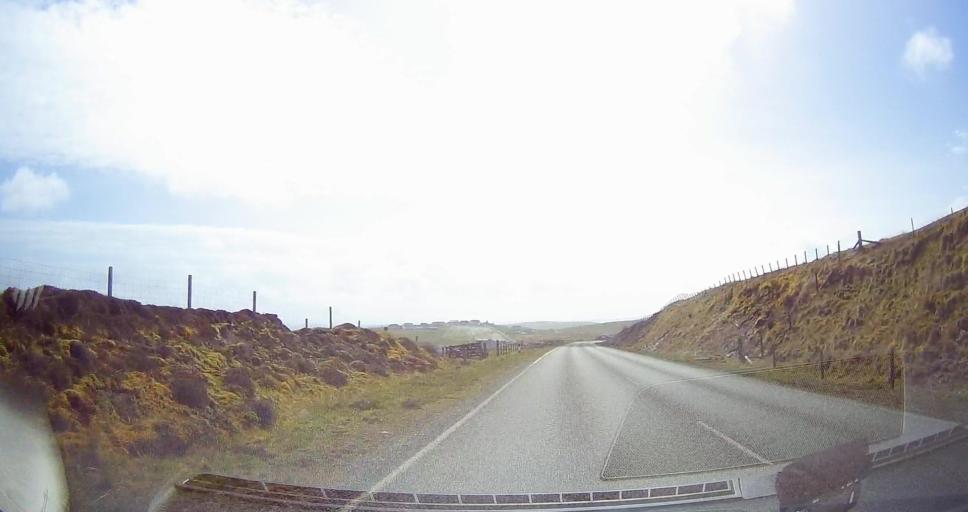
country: GB
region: Scotland
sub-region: Shetland Islands
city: Sandwick
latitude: 60.0668
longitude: -1.2246
